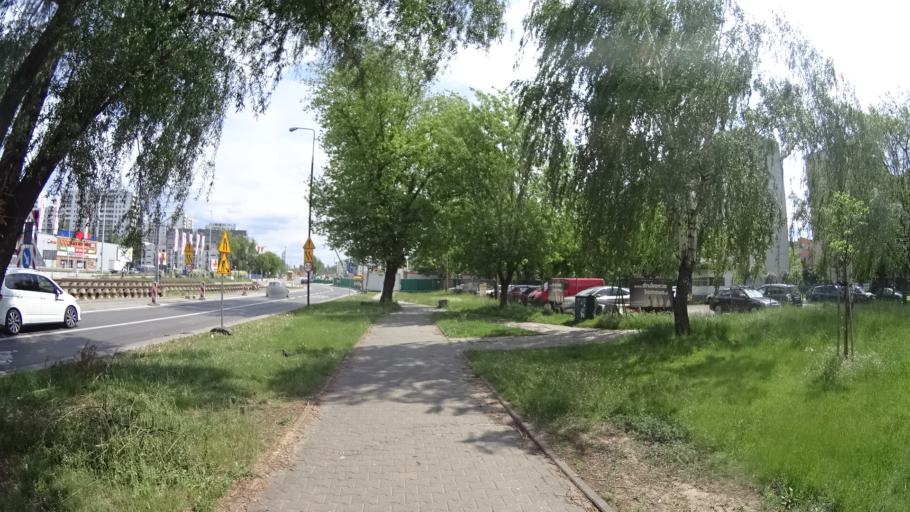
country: PL
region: Masovian Voivodeship
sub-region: Warszawa
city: Bemowo
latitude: 52.2387
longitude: 20.9059
